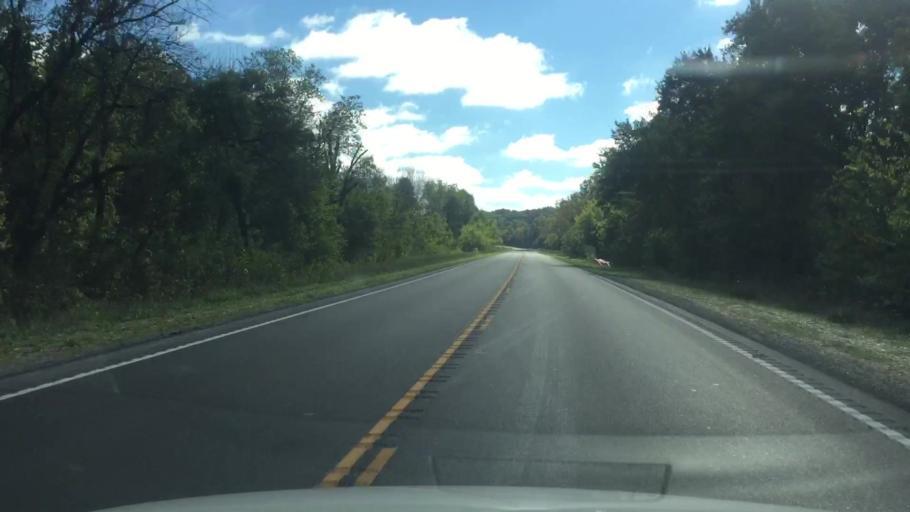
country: US
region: Missouri
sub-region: Howard County
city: New Franklin
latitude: 38.9871
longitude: -92.5545
